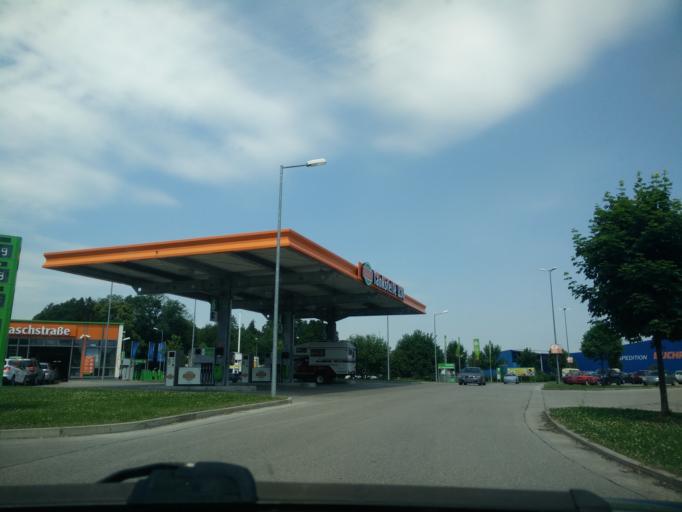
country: DE
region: Bavaria
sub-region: Upper Bavaria
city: Ainring
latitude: 47.8251
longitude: 12.9611
